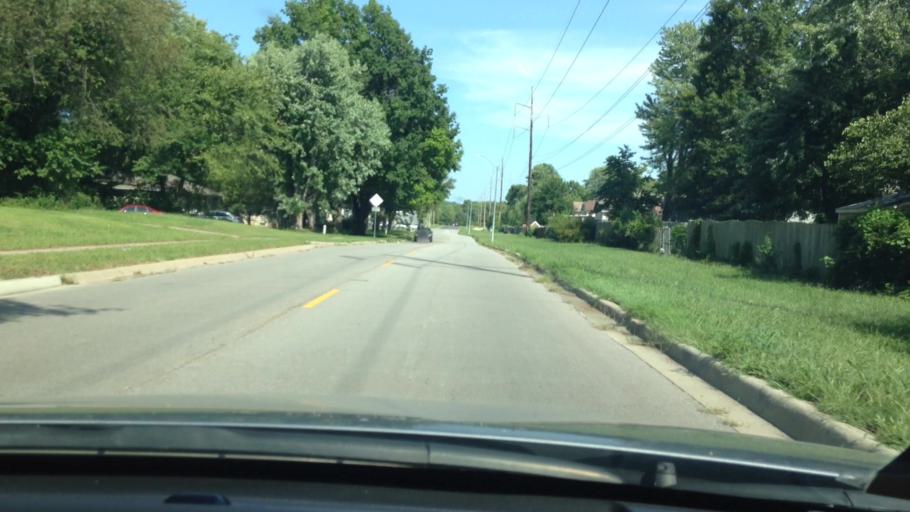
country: US
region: Missouri
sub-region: Jackson County
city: Grandview
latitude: 38.8719
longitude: -94.5166
